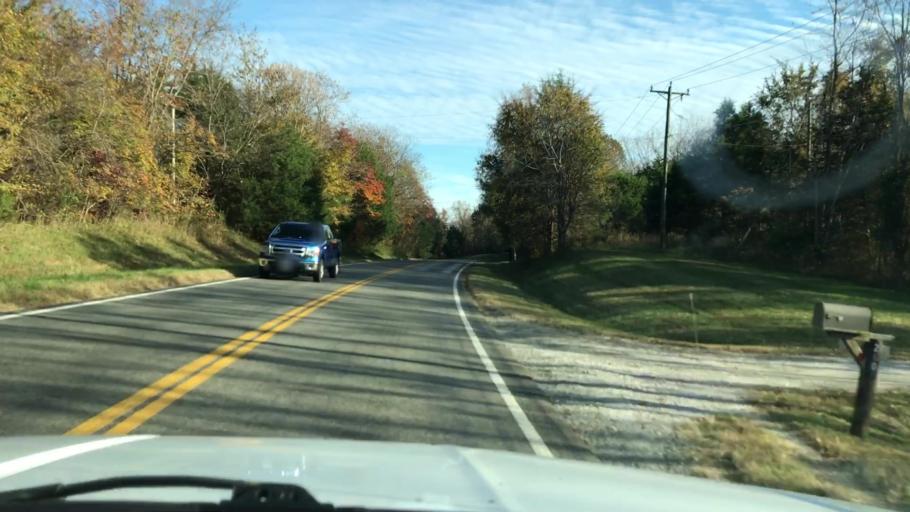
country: US
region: Virginia
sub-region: Goochland County
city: Goochland
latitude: 37.6647
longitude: -77.8726
